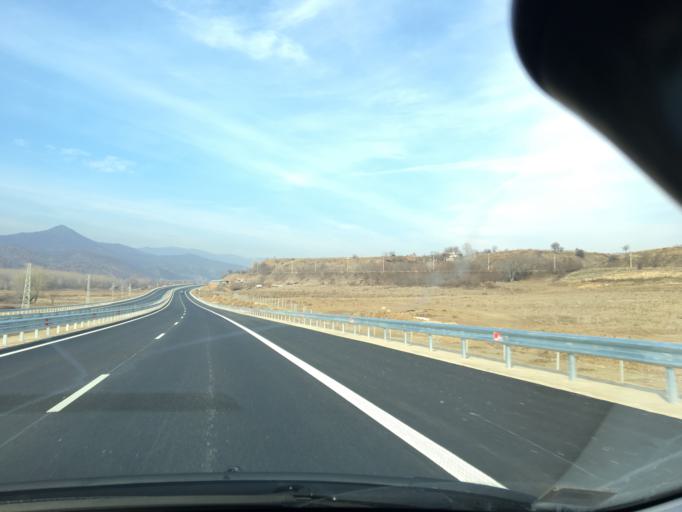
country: BG
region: Blagoevgrad
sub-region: Obshtina Sandanski
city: Sandanski
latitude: 41.5544
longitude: 23.2484
